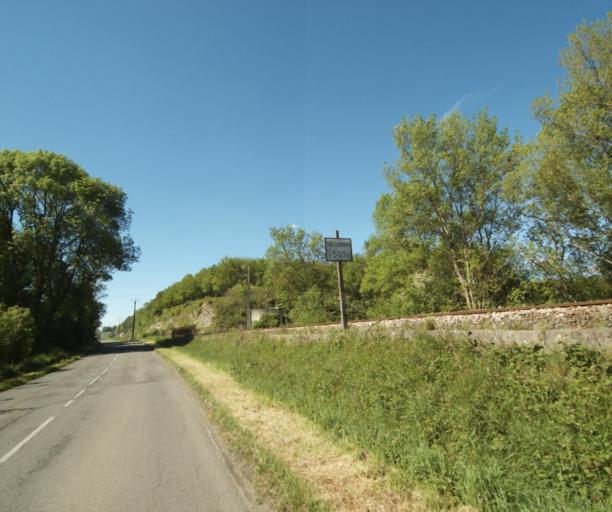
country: FR
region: Poitou-Charentes
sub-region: Departement de la Charente-Maritime
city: Bussac-sur-Charente
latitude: 45.8260
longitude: -0.6407
